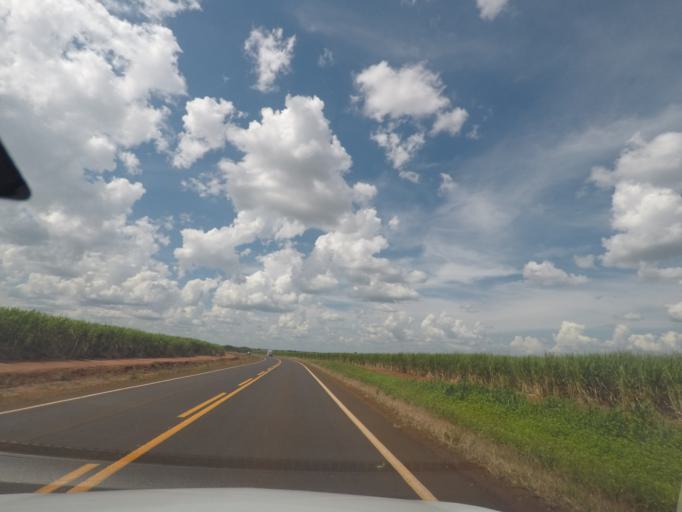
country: BR
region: Minas Gerais
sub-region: Conceicao Das Alagoas
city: Conceicao das Alagoas
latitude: -19.8403
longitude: -48.5918
